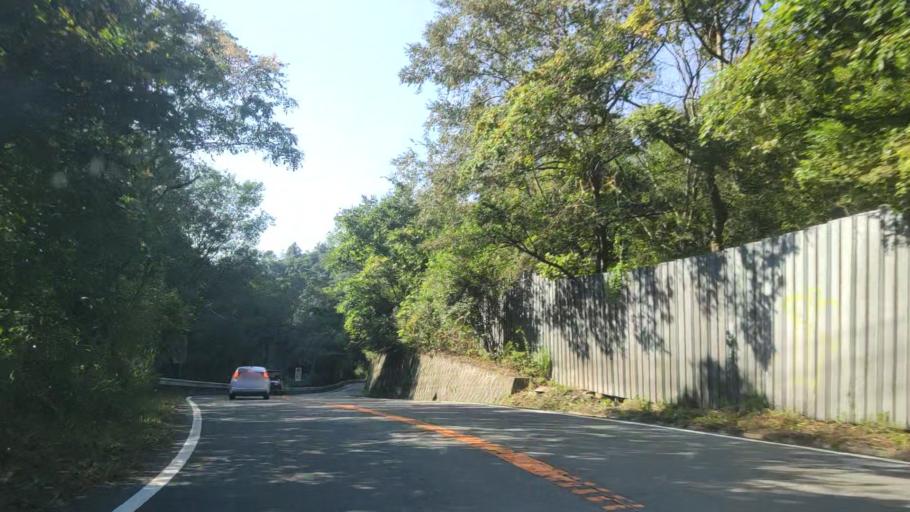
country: JP
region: Hyogo
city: Kobe
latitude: 34.7124
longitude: 135.1596
